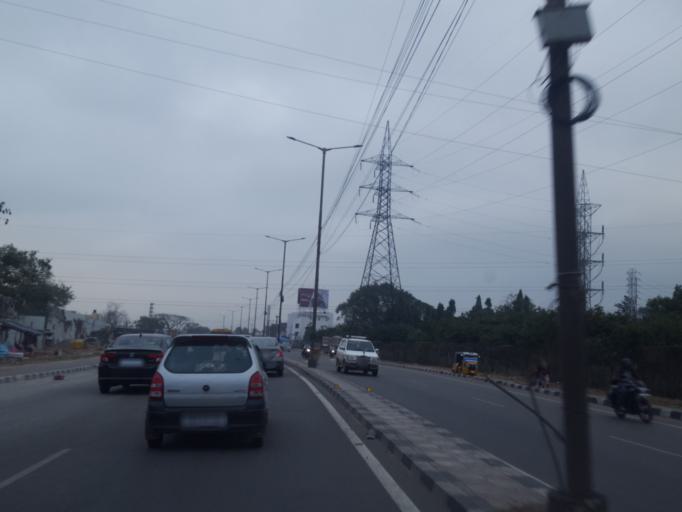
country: IN
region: Telangana
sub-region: Medak
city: Patancheru
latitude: 17.5161
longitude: 78.2824
